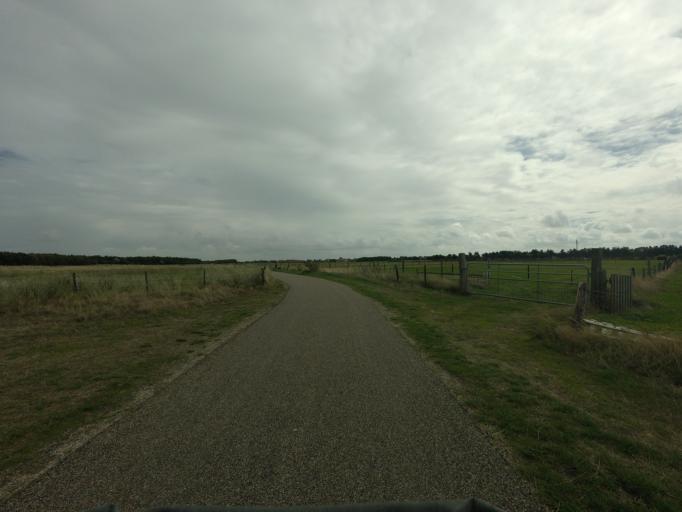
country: NL
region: Friesland
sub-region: Gemeente Ameland
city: Nes
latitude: 53.4524
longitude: 5.7873
